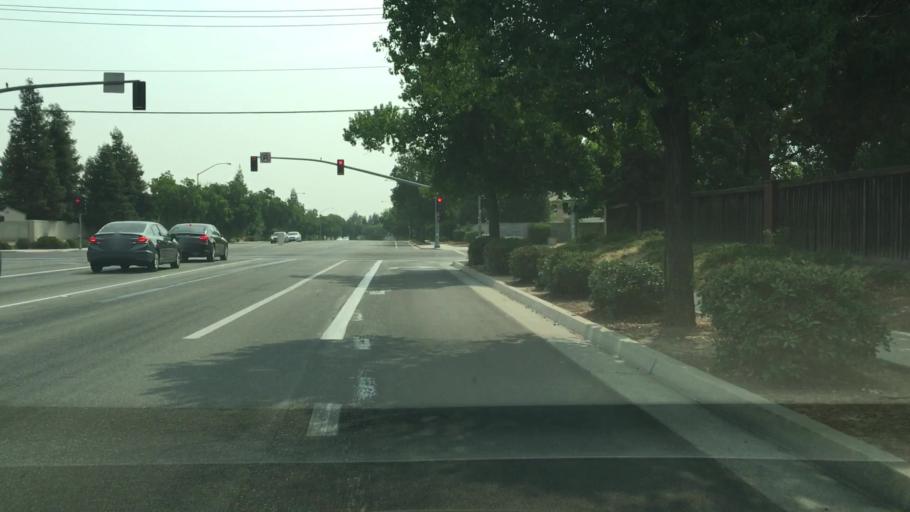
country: US
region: California
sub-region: Fresno County
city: Clovis
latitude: 36.8738
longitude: -119.7483
